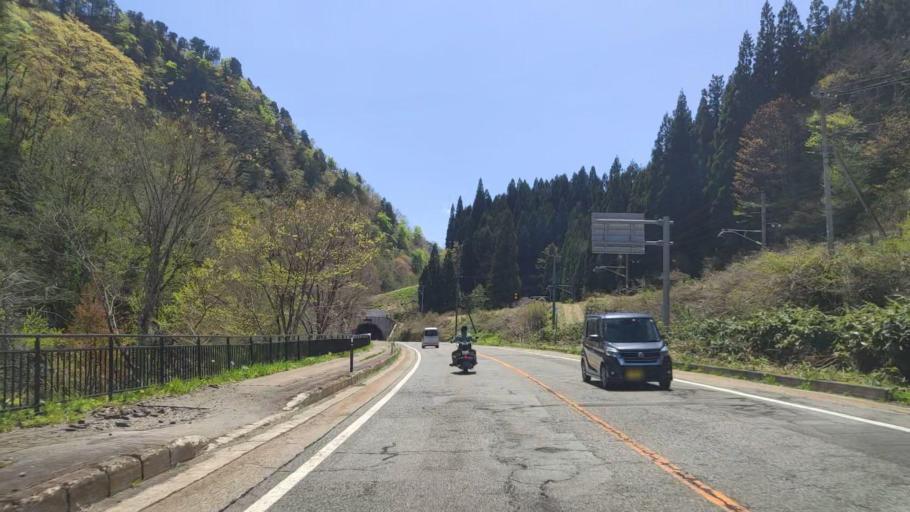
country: JP
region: Akita
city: Yuzawa
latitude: 38.9881
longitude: 140.3625
